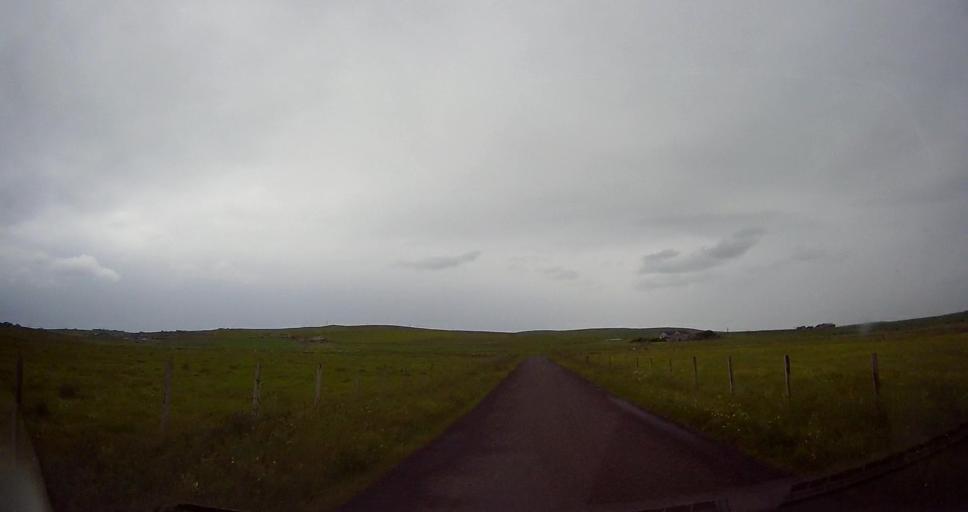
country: GB
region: Scotland
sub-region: Orkney Islands
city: Stromness
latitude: 59.0685
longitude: -3.2811
